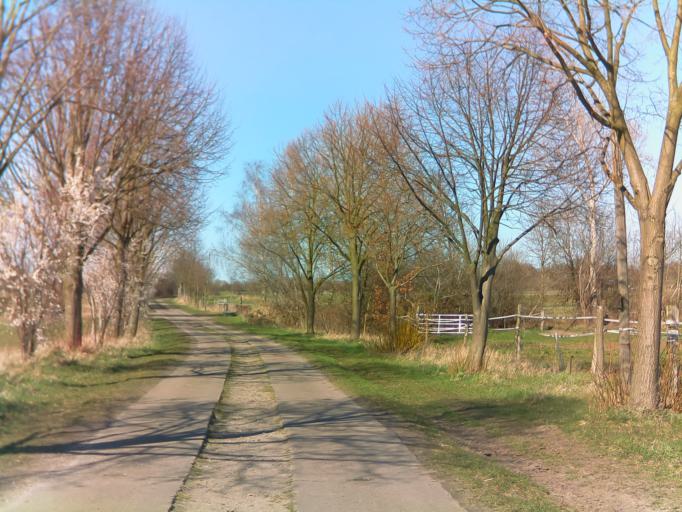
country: DE
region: Brandenburg
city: Werder
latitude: 52.4365
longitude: 12.9558
